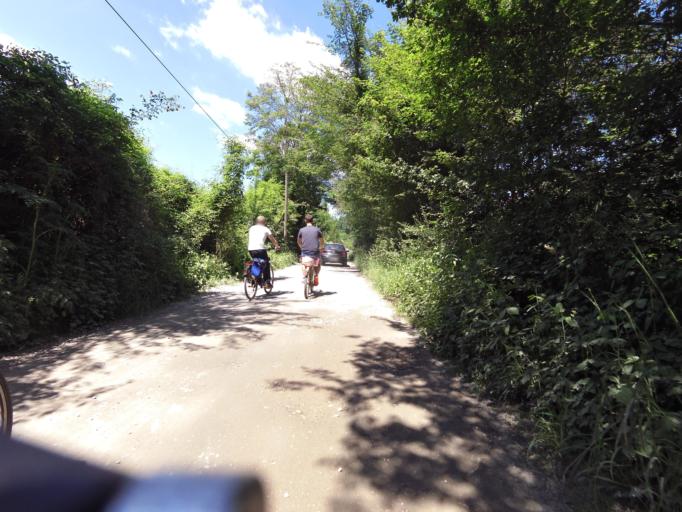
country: DE
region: Rheinland-Pfalz
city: Nackenheim
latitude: 49.9263
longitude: 8.3526
